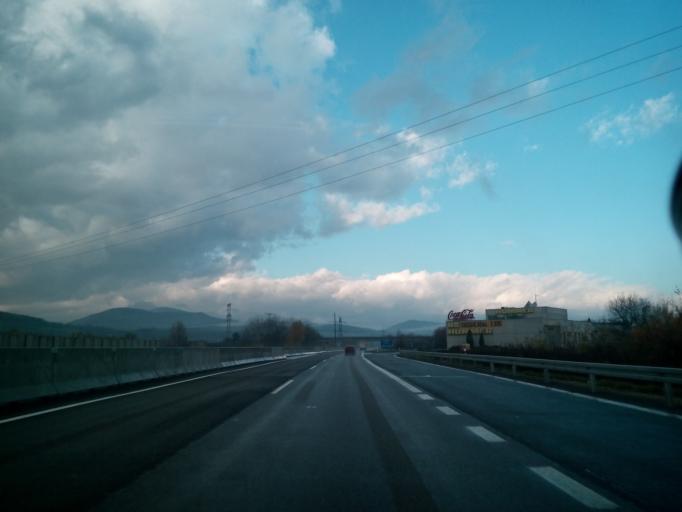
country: SK
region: Kosicky
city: Kosice
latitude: 48.8553
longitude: 21.2725
